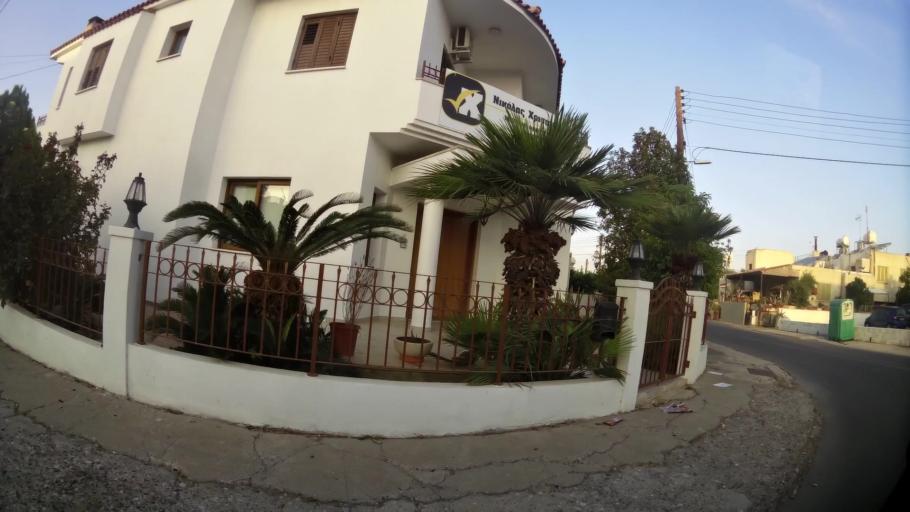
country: CY
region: Larnaka
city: Aradippou
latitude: 34.9221
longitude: 33.5915
